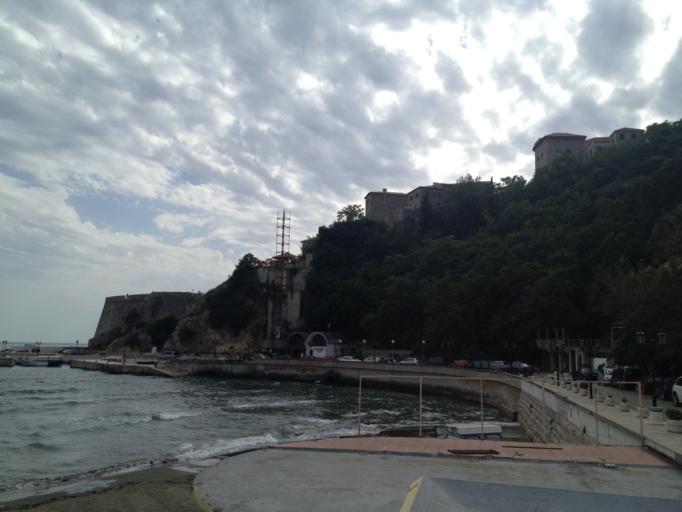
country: ME
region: Ulcinj
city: Ulcinj
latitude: 41.9245
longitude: 19.2037
